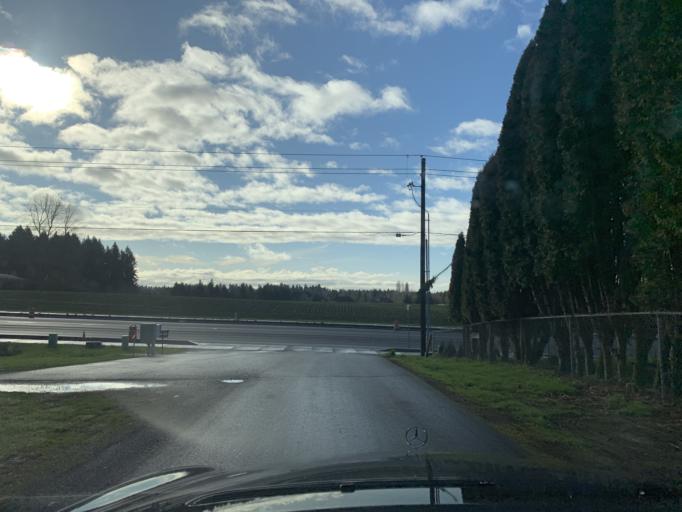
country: US
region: Washington
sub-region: Clark County
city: Five Corners
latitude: 45.7083
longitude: -122.5670
